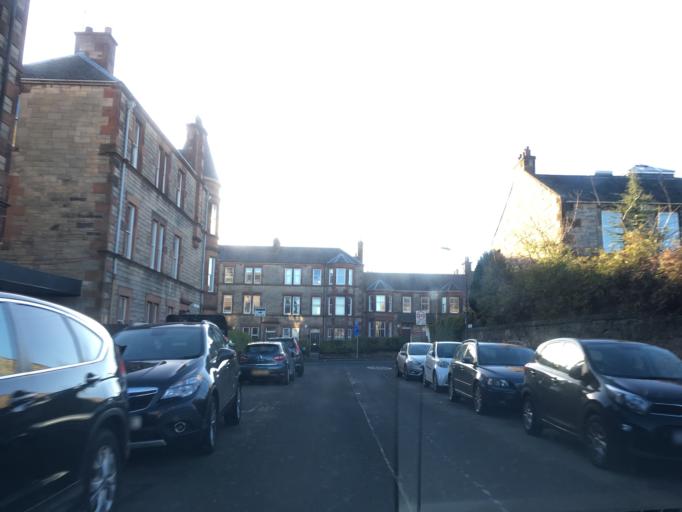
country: GB
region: Scotland
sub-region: Edinburgh
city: Colinton
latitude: 55.9582
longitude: -3.2501
